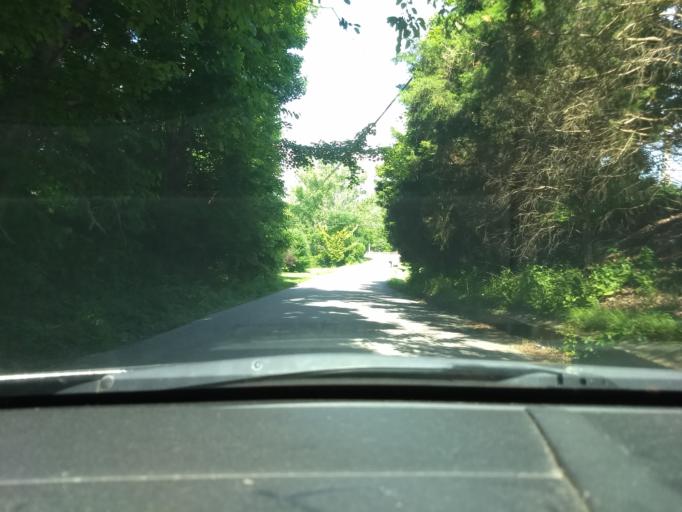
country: US
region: Indiana
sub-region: Floyd County
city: New Albany
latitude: 38.2682
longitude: -85.8469
